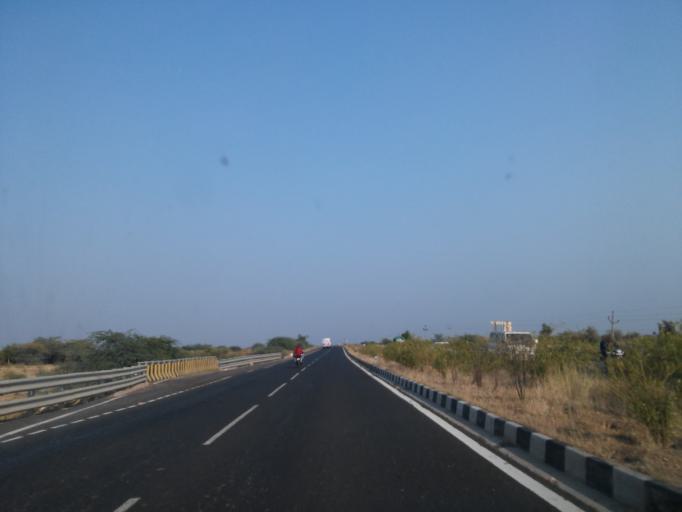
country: IN
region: Gujarat
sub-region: Surendranagar
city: Dhrangadhra
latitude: 23.0246
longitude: 71.6306
